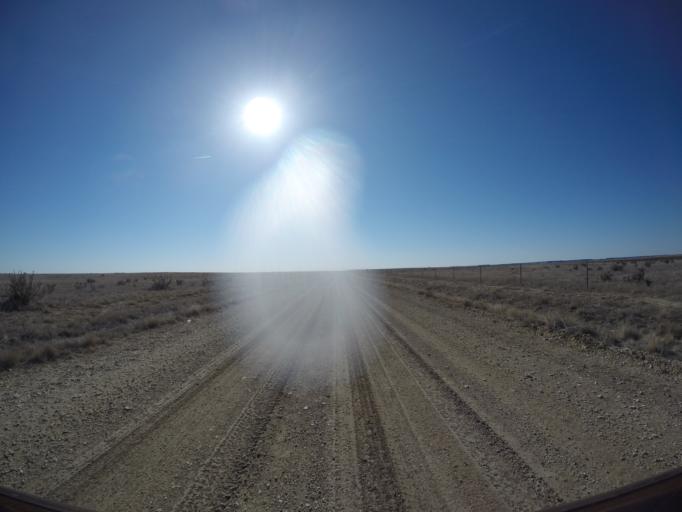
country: US
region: Colorado
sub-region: Otero County
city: La Junta
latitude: 37.6846
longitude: -103.6204
